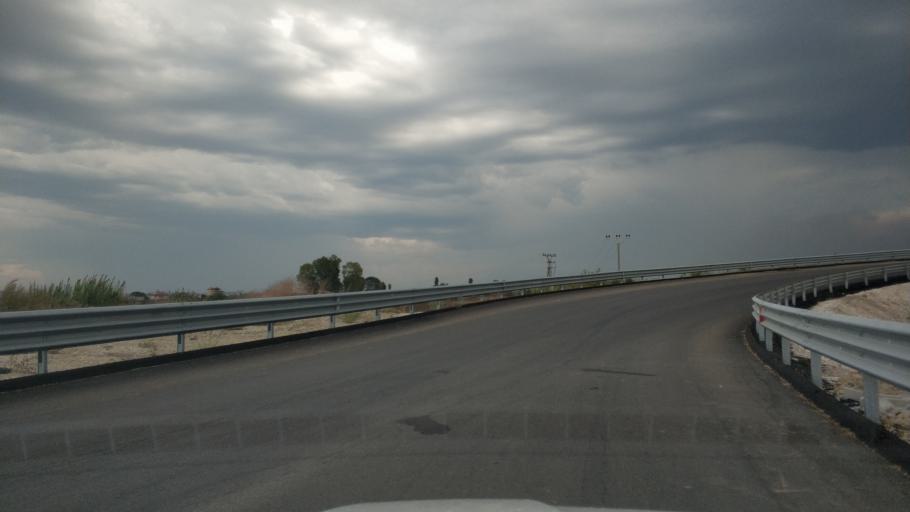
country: AL
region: Fier
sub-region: Rrethi i Fierit
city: Dermenas
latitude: 40.7417
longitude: 19.4823
